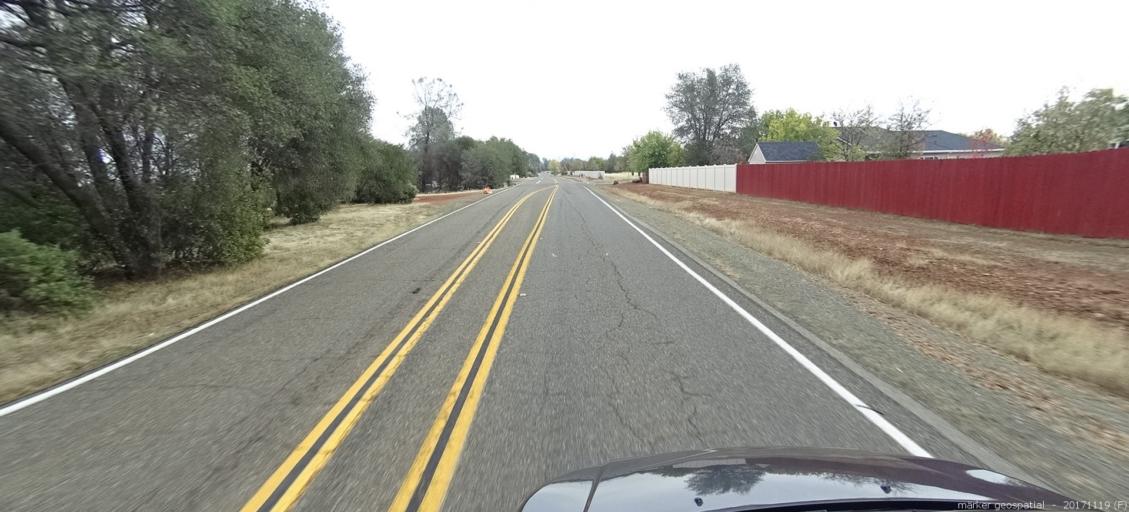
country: US
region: California
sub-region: Shasta County
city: Redding
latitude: 40.4881
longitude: -122.4394
